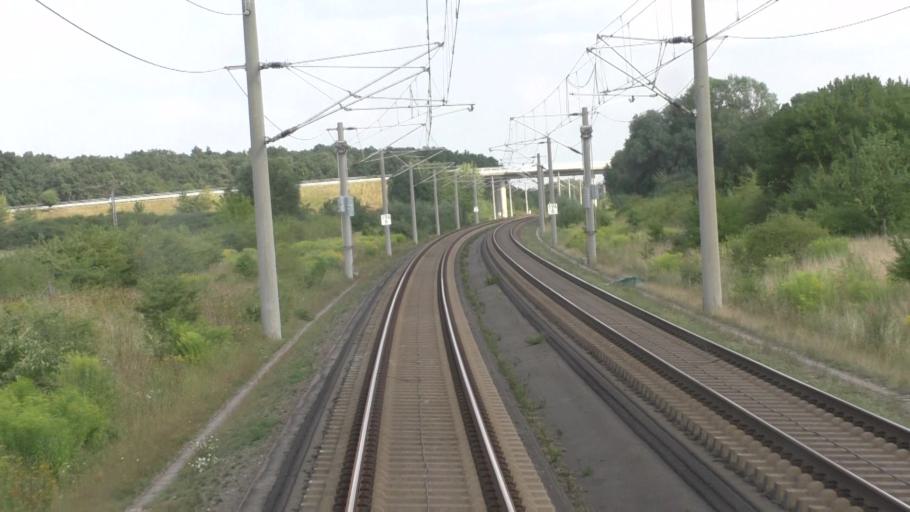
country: DE
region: Saxony-Anhalt
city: Tangermunde
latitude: 52.6008
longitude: 11.9731
